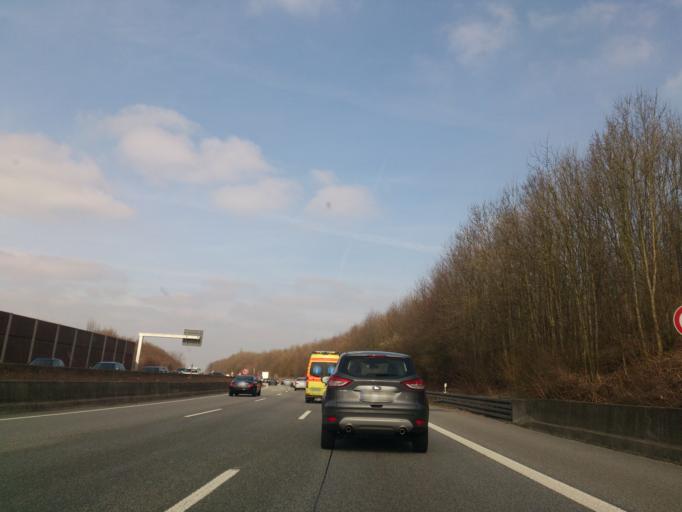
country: DE
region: North Rhine-Westphalia
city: Haan
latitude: 51.2129
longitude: 7.0540
